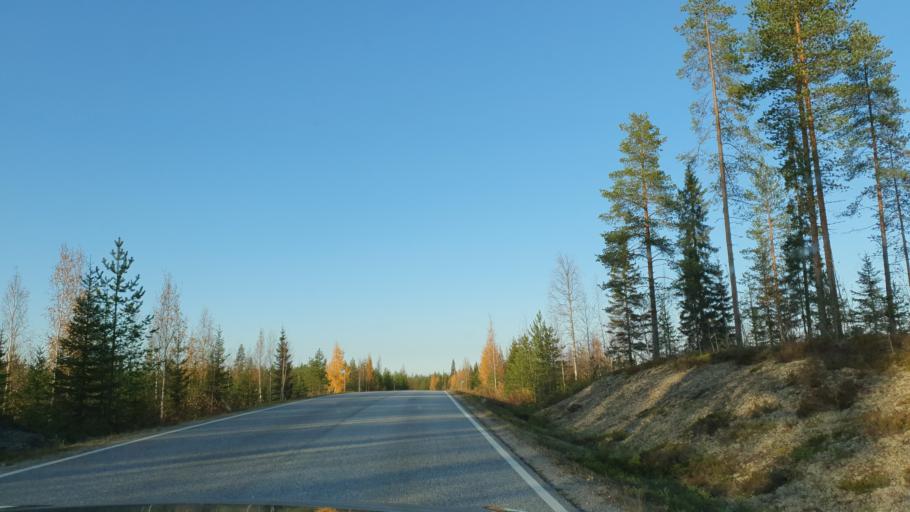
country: FI
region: Kainuu
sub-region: Kehys-Kainuu
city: Kuhmo
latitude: 64.3662
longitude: 29.4892
